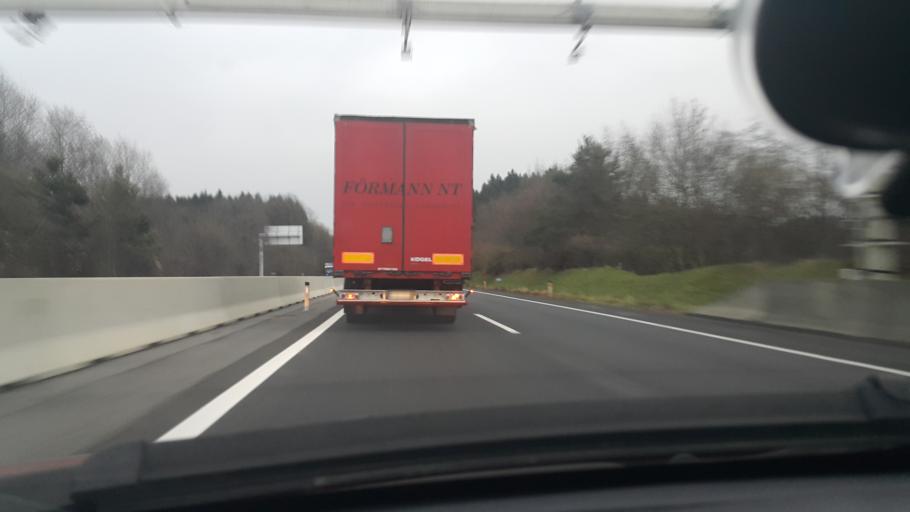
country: AT
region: Carinthia
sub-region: Politischer Bezirk Volkermarkt
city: Voelkermarkt
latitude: 46.6781
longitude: 14.6140
